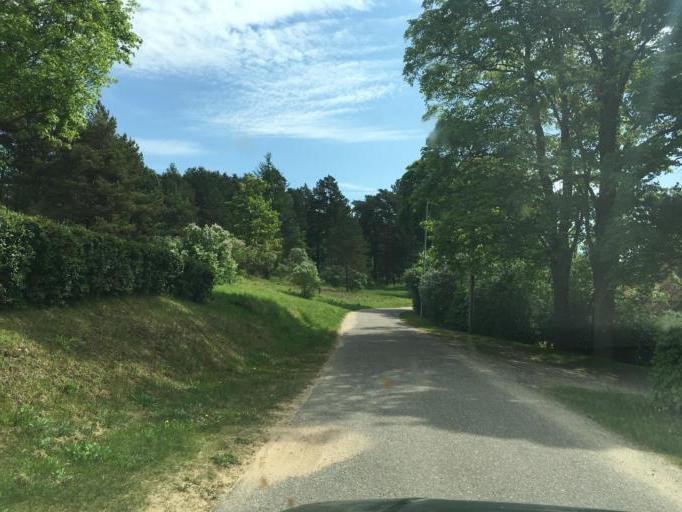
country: LV
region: Talsu Rajons
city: Valdemarpils
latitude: 57.3692
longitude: 22.5951
